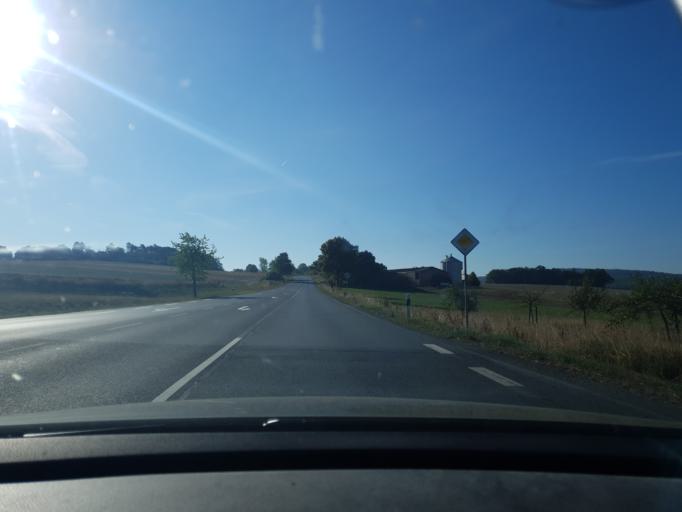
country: DE
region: Hesse
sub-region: Regierungsbezirk Giessen
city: Hoernsheim
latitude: 50.4739
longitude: 8.6266
